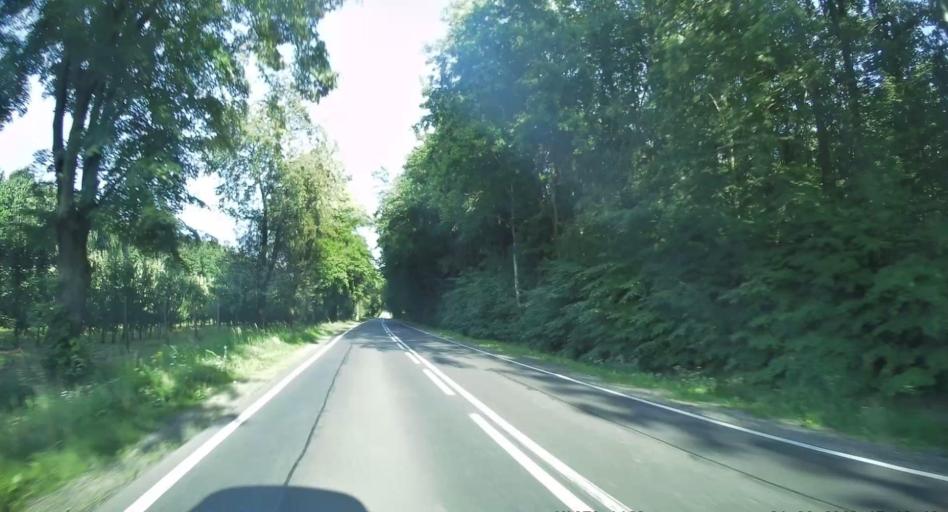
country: PL
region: Lodz Voivodeship
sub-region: Powiat rawski
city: Sadkowice
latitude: 51.8052
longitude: 20.5831
